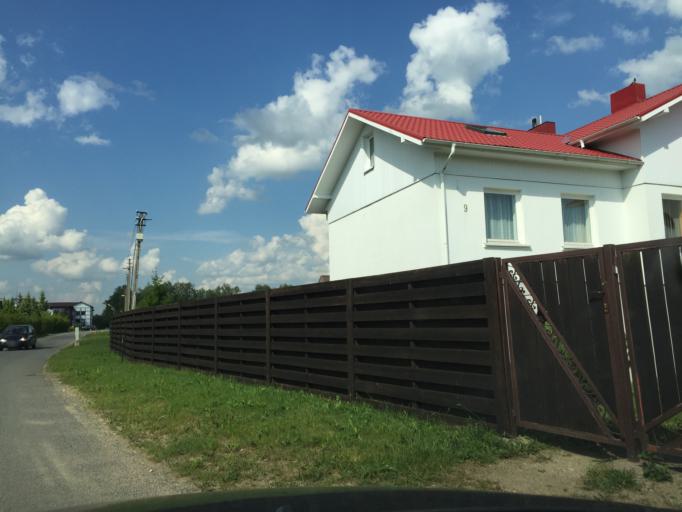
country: LT
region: Klaipedos apskritis
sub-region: Klaipeda
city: Palanga
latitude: 55.9061
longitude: 21.1237
